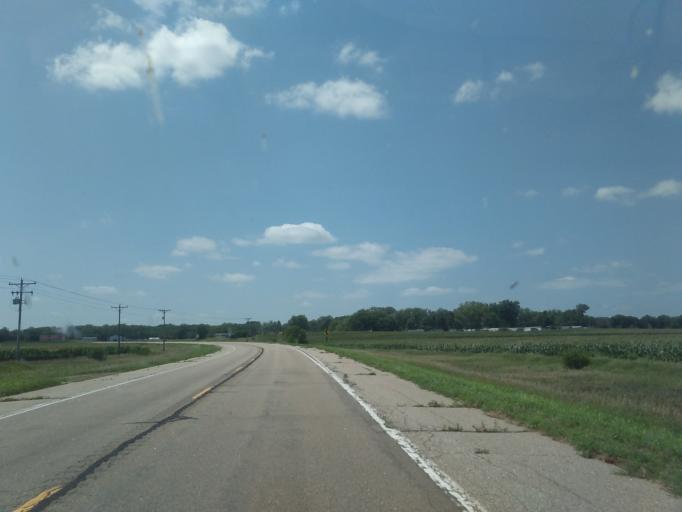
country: US
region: Nebraska
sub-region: Gosper County
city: Elwood
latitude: 40.6847
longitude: -99.8201
